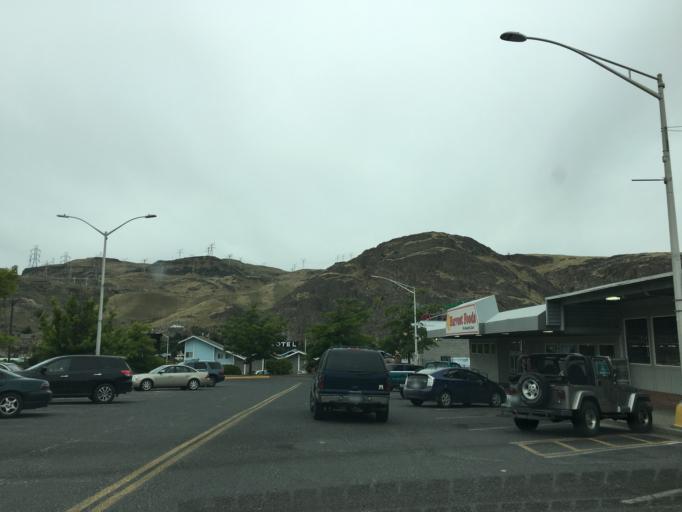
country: US
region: Washington
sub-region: Okanogan County
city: Coulee Dam
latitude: 47.9662
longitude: -118.9765
